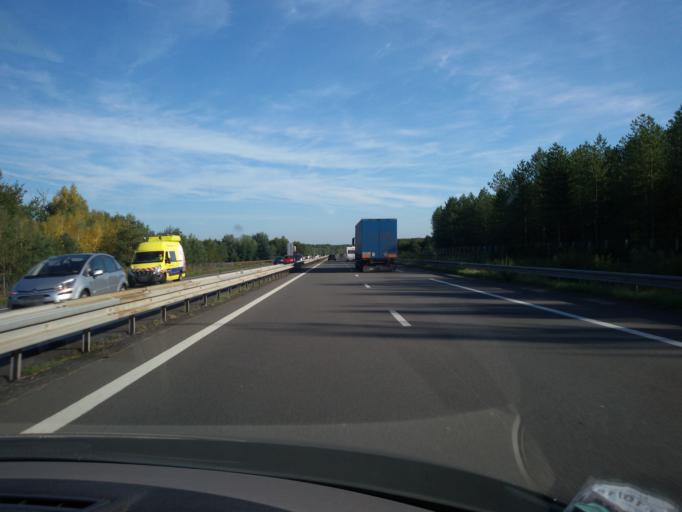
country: FR
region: Centre
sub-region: Departement du Loir-et-Cher
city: Theillay
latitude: 47.3271
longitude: 2.0488
